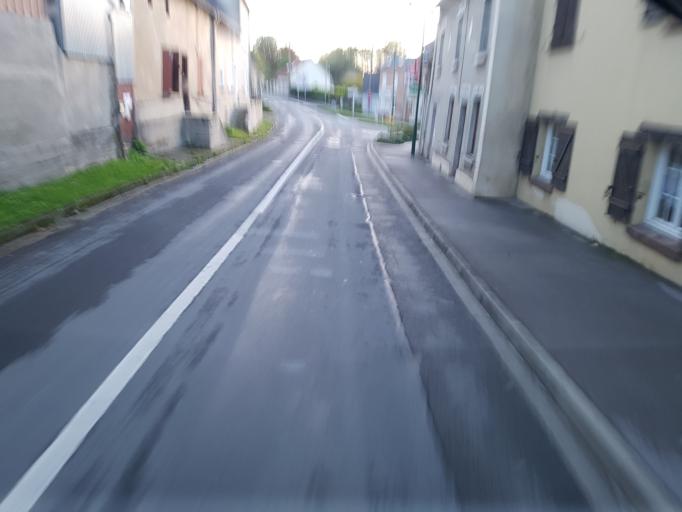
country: FR
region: Picardie
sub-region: Departement de la Somme
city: Saleux
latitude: 49.8156
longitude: 2.2202
